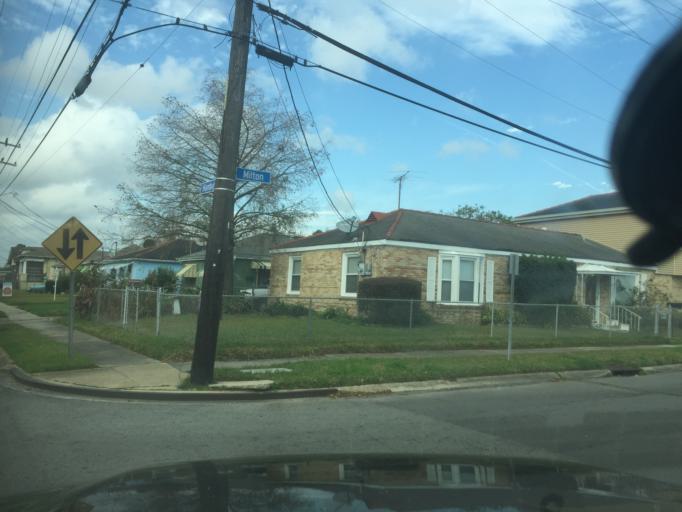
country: US
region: Louisiana
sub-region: Orleans Parish
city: New Orleans
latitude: 29.9960
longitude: -90.0748
